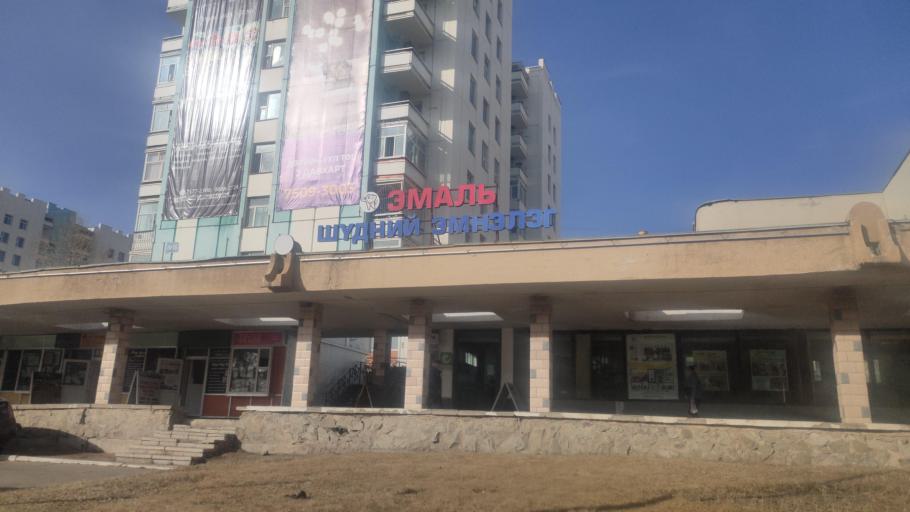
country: MN
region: Orhon
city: Erdenet
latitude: 49.0292
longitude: 104.0507
